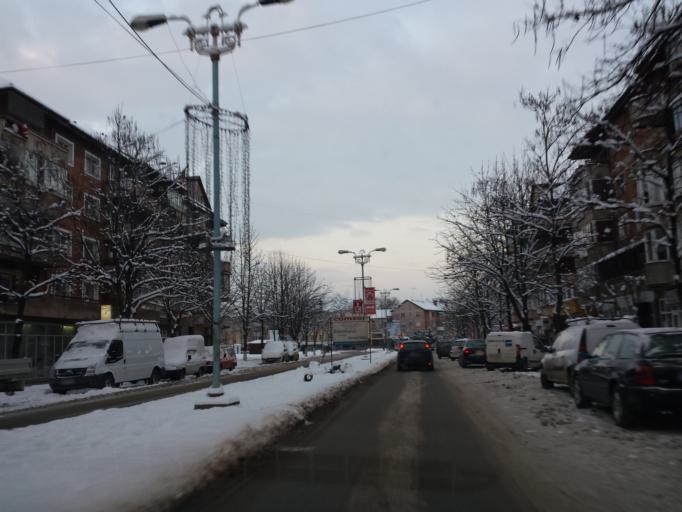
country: RO
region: Hunedoara
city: Hunedoara
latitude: 45.7546
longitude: 22.8990
